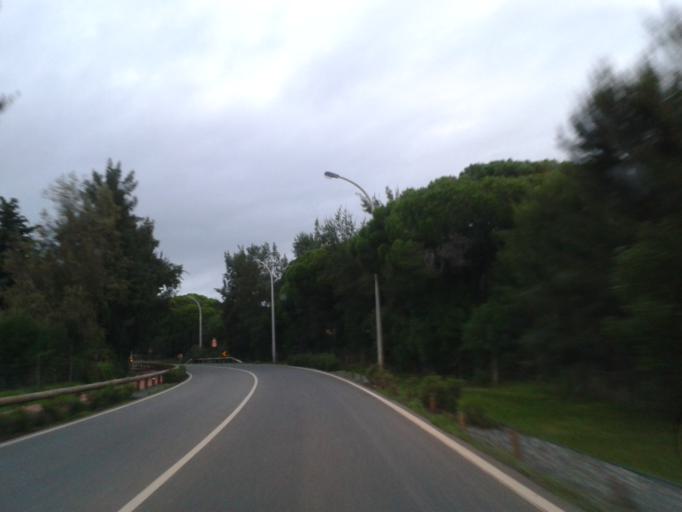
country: PT
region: Faro
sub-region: Loule
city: Boliqueime
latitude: 37.1071
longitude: -8.1378
